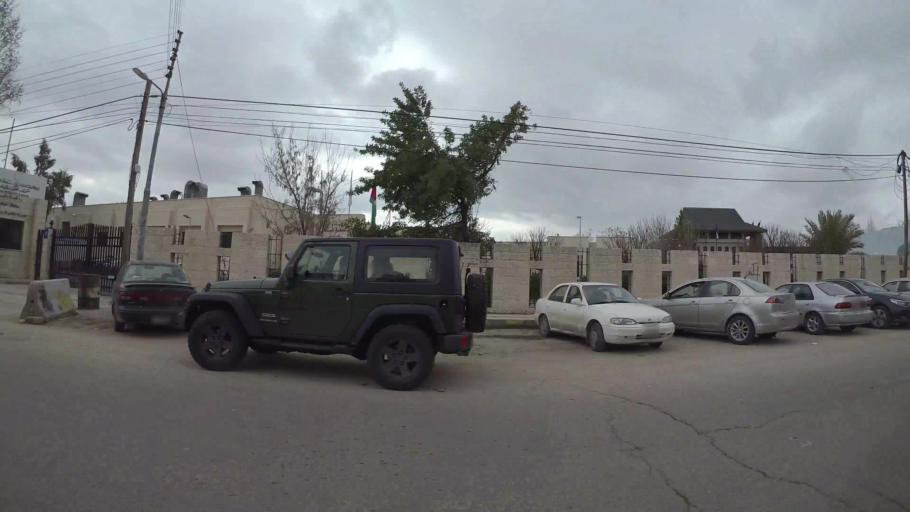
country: JO
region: Amman
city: Wadi as Sir
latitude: 31.9450
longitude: 35.8319
